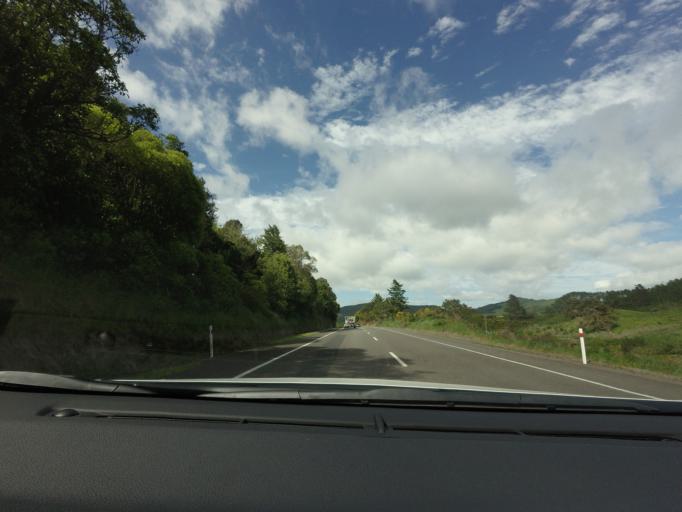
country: NZ
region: Bay of Plenty
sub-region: Rotorua District
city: Rotorua
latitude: -38.3301
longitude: 176.3688
